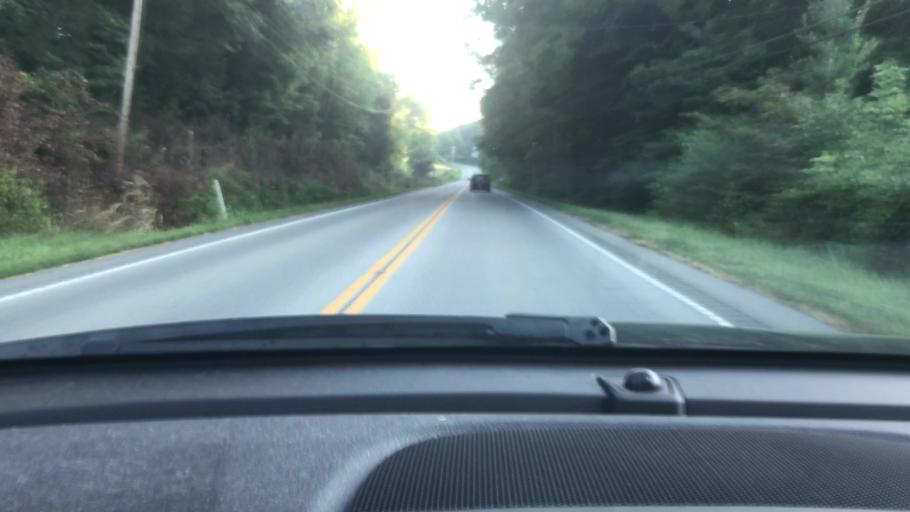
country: US
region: Tennessee
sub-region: Dickson County
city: Dickson
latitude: 36.1176
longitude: -87.3657
